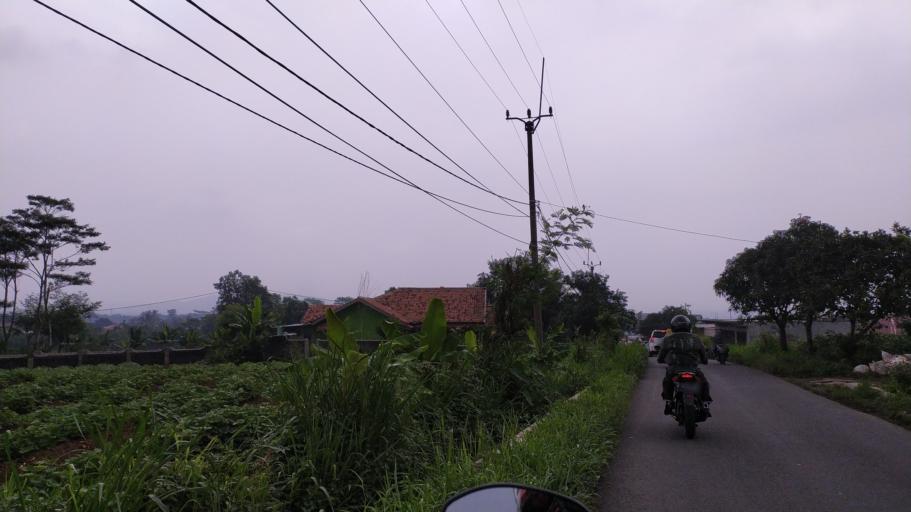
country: ID
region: West Java
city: Ciampea
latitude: -6.6082
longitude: 106.6991
